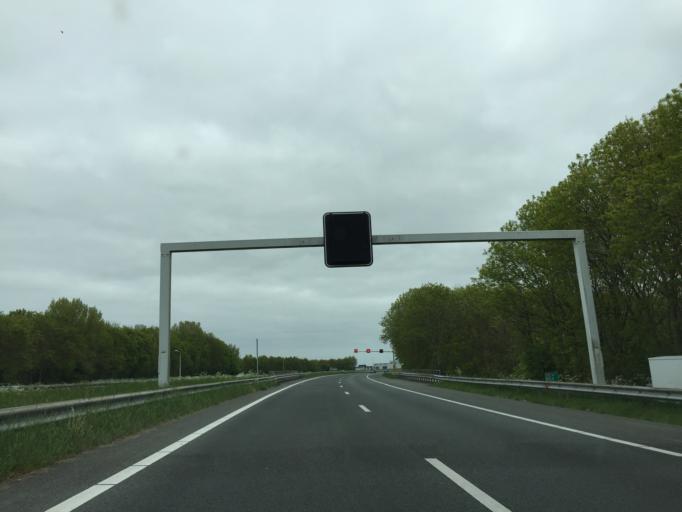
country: NL
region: North Holland
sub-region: Gemeente Hollands Kroon
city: Den Oever
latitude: 52.9283
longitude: 5.0353
